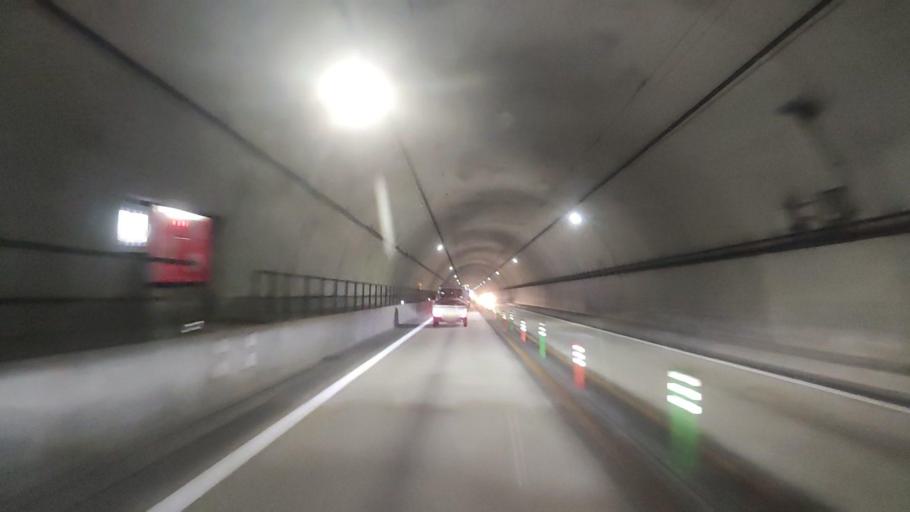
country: JP
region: Wakayama
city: Tanabe
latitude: 33.6068
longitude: 135.4283
